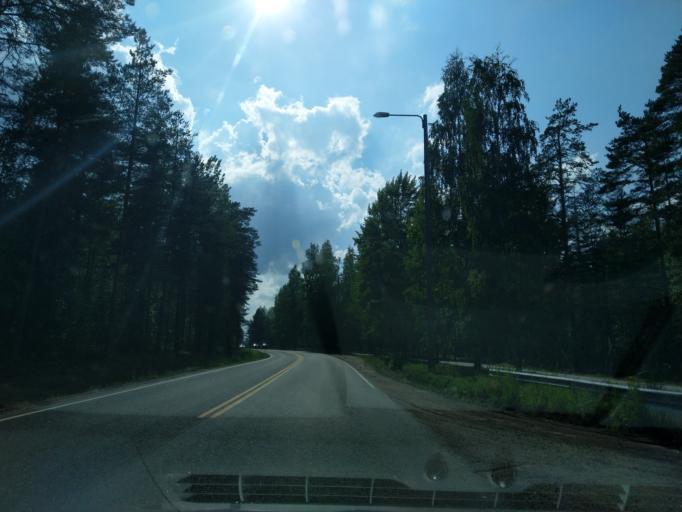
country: FI
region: Kymenlaakso
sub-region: Kouvola
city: Kouvola
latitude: 60.8848
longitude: 26.7841
